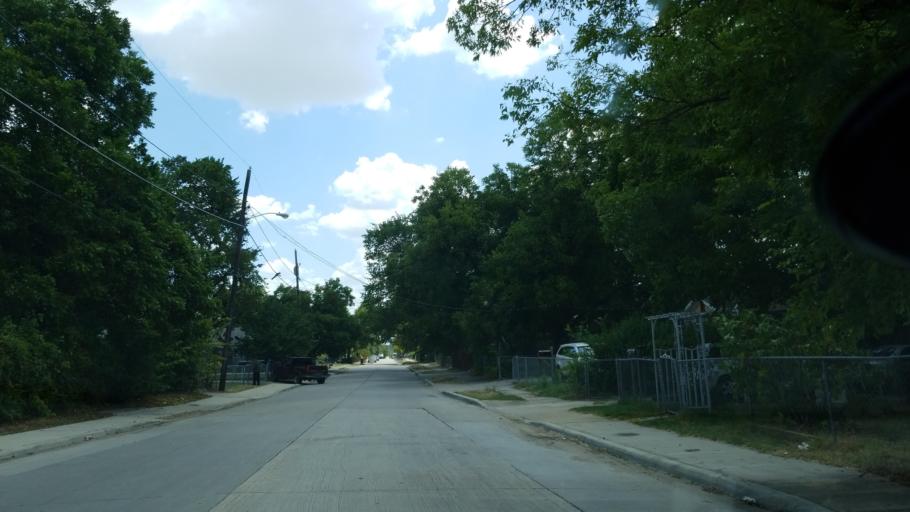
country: US
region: Texas
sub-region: Dallas County
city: Cockrell Hill
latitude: 32.7491
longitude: -96.9088
